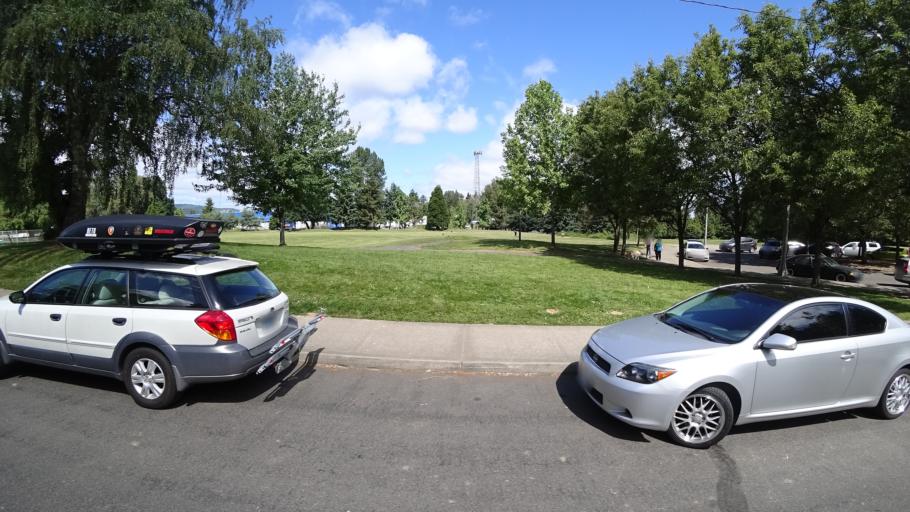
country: US
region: Oregon
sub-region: Washington County
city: West Haven
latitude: 45.6031
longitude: -122.7585
